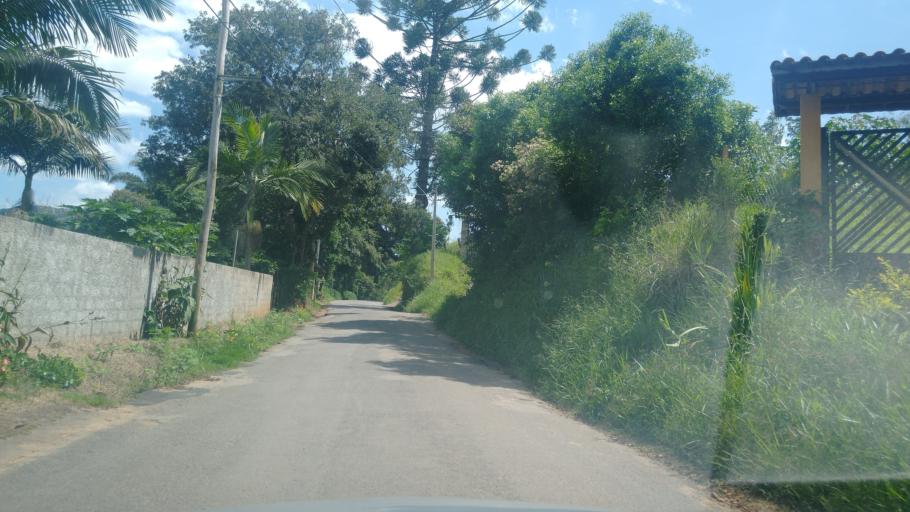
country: BR
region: Minas Gerais
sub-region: Extrema
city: Extrema
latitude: -22.7779
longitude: -46.2855
